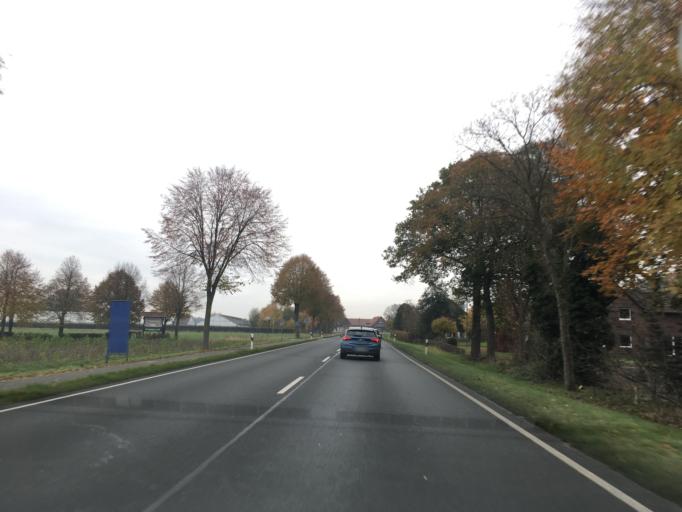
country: DE
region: North Rhine-Westphalia
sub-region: Regierungsbezirk Munster
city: Telgte
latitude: 51.9927
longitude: 7.8036
